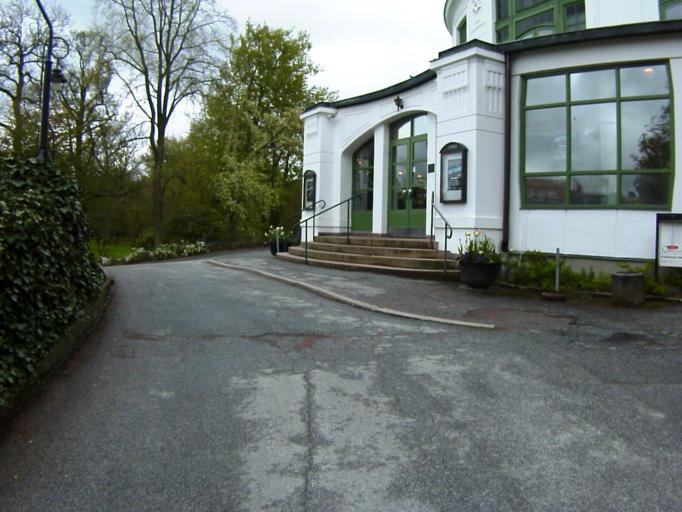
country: SE
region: Skane
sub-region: Kristianstads Kommun
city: Kristianstad
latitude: 56.0277
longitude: 14.1535
